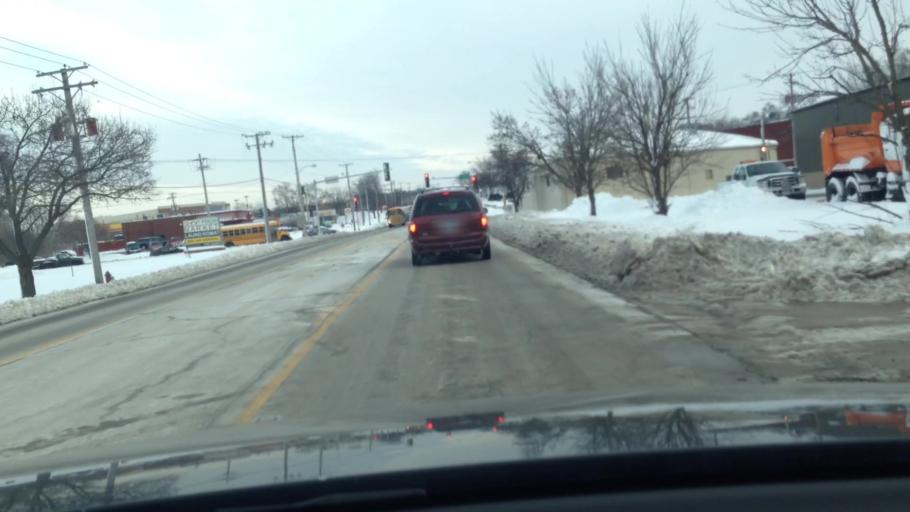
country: US
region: Illinois
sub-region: McHenry County
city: Woodstock
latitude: 42.3165
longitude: -88.4396
